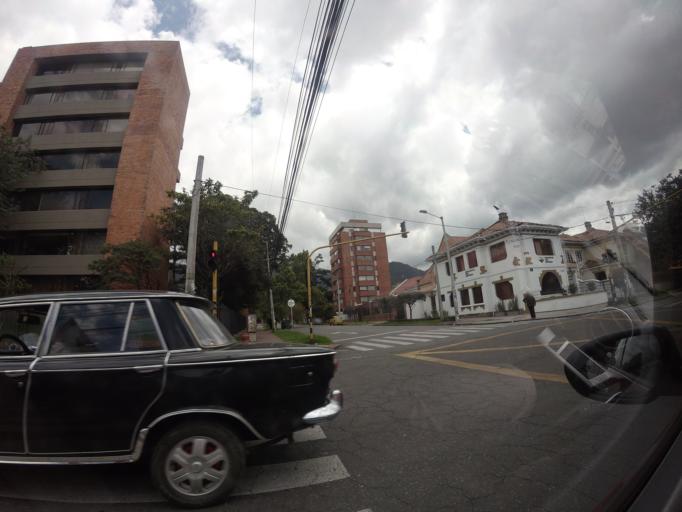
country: CO
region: Bogota D.C.
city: Barrio San Luis
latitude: 4.6612
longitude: -74.0585
